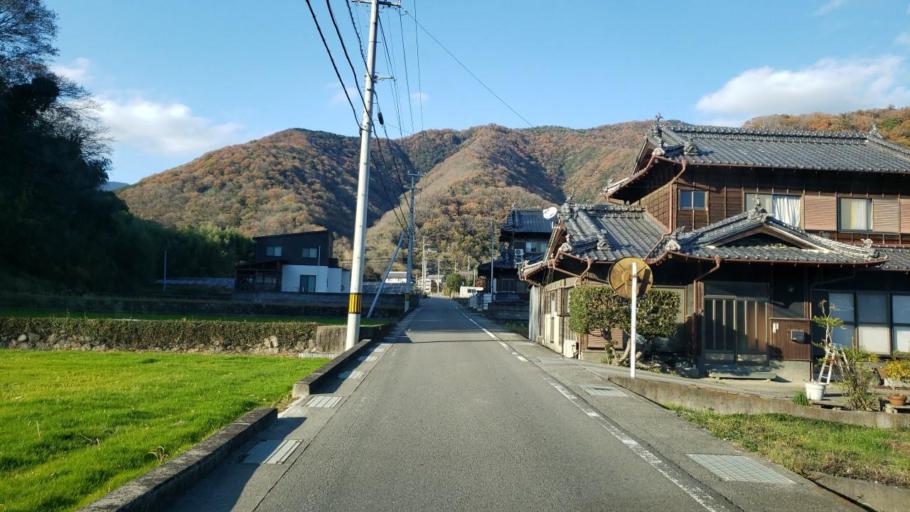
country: JP
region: Tokushima
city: Wakimachi
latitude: 34.0719
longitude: 134.0843
